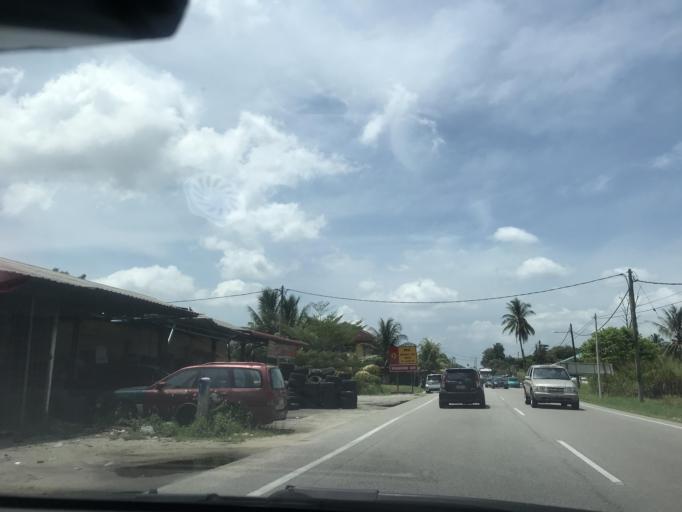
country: MY
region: Kelantan
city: Kota Bharu
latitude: 6.1478
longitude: 102.2164
